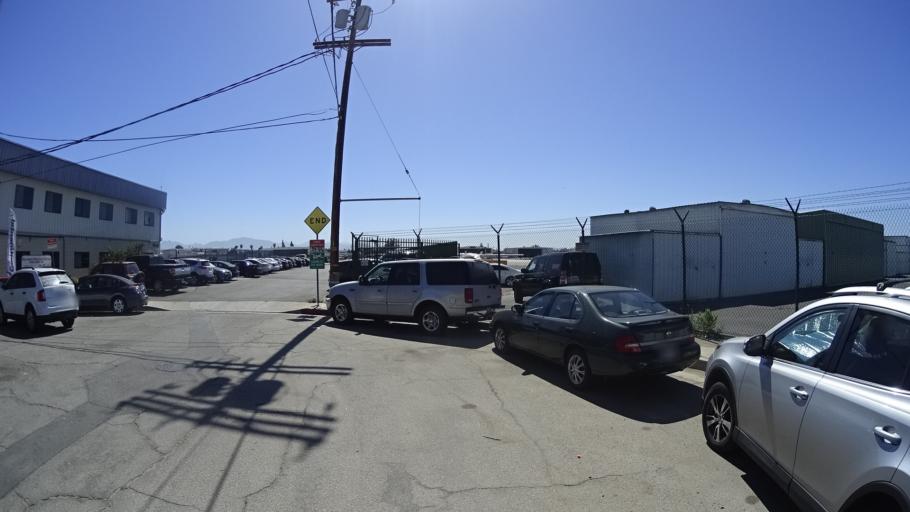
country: US
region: California
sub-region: Los Angeles County
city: Van Nuys
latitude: 34.1975
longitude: -118.4913
